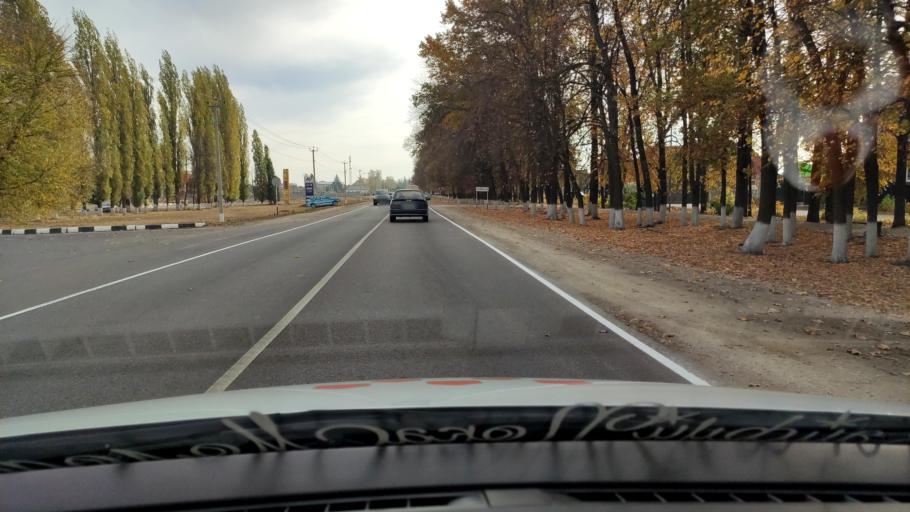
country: RU
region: Voronezj
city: Ramon'
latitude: 51.9127
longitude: 39.3204
